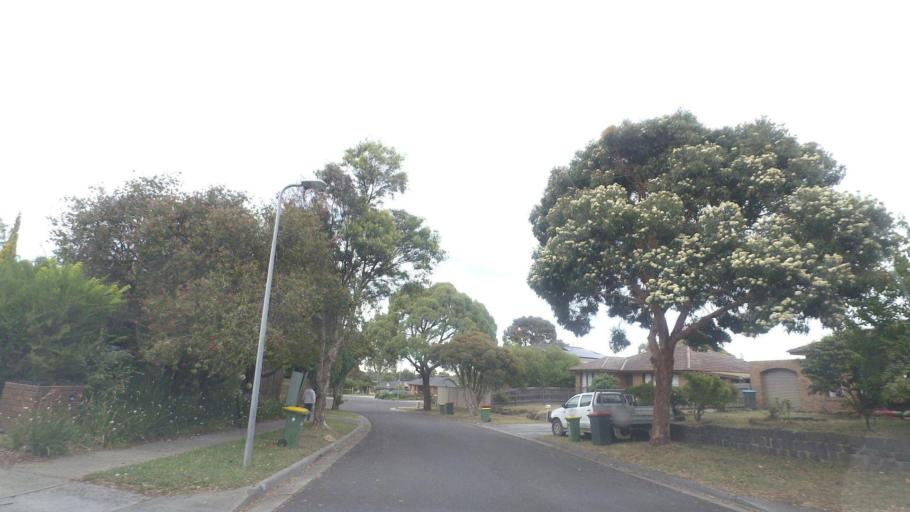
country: AU
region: Victoria
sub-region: Knox
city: Wantirna
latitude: -37.8597
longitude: 145.2295
